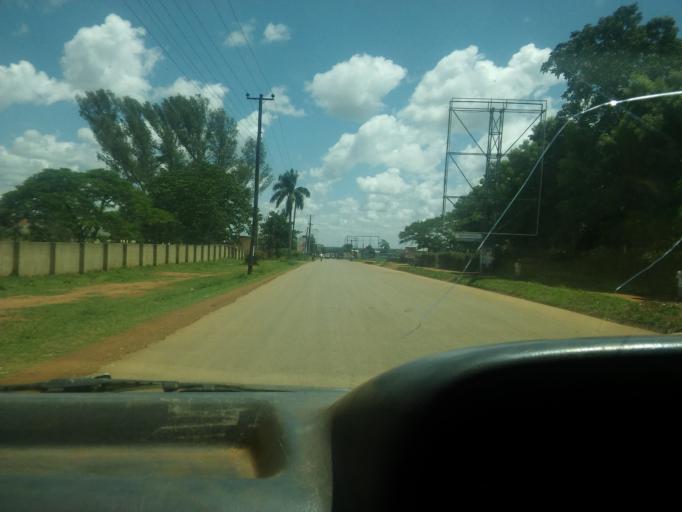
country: UG
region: Eastern Region
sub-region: Mbale District
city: Mbale
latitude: 1.0795
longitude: 34.1605
